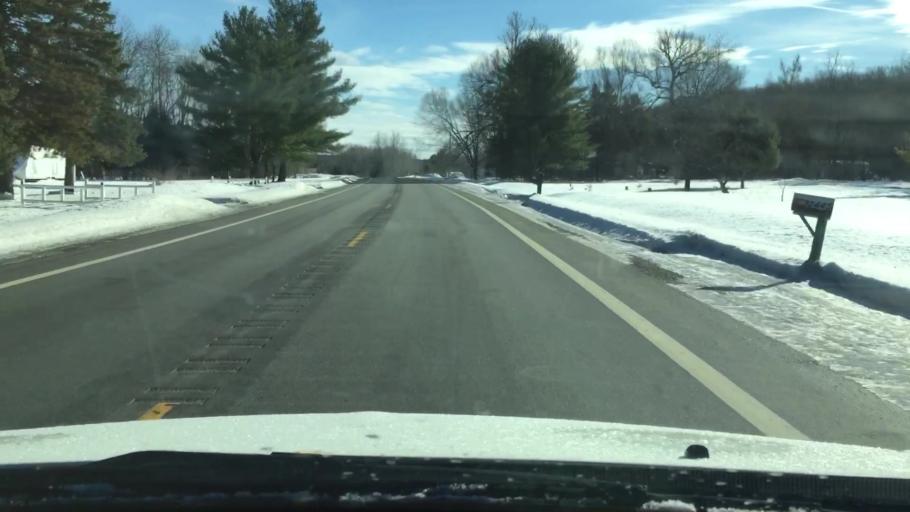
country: US
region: Michigan
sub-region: Charlevoix County
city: East Jordan
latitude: 45.0669
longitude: -85.0836
